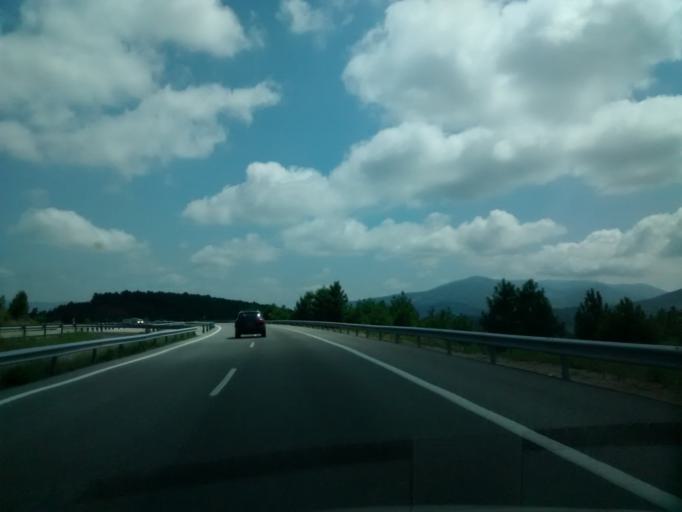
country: ES
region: Castille and Leon
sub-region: Provincia de Leon
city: Ponferrada
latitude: 42.5608
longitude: -6.5571
